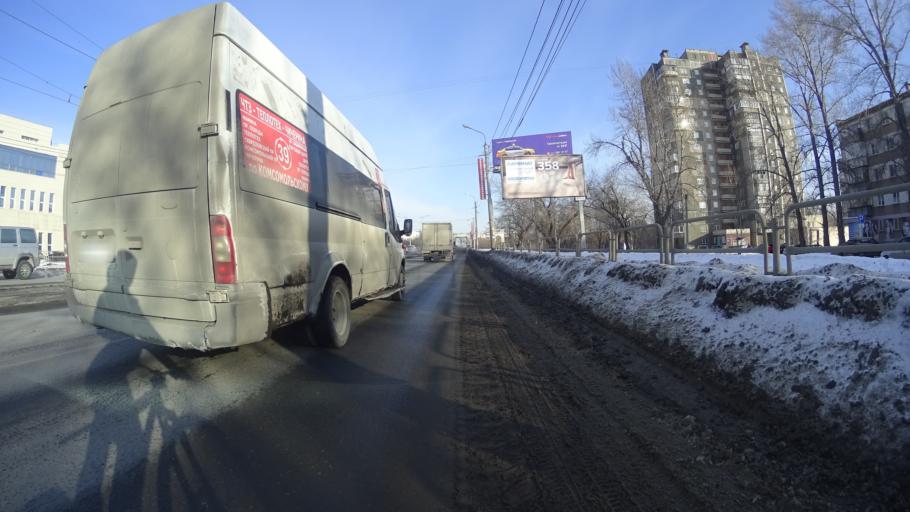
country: RU
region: Chelyabinsk
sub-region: Gorod Chelyabinsk
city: Chelyabinsk
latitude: 55.1846
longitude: 61.4069
